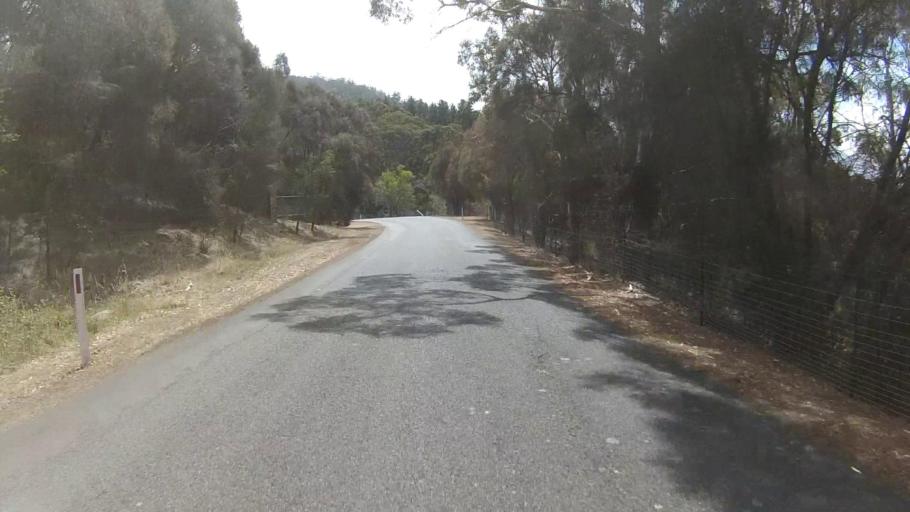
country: AU
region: Tasmania
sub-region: Kingborough
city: Blackmans Bay
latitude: -43.0448
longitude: 147.3351
